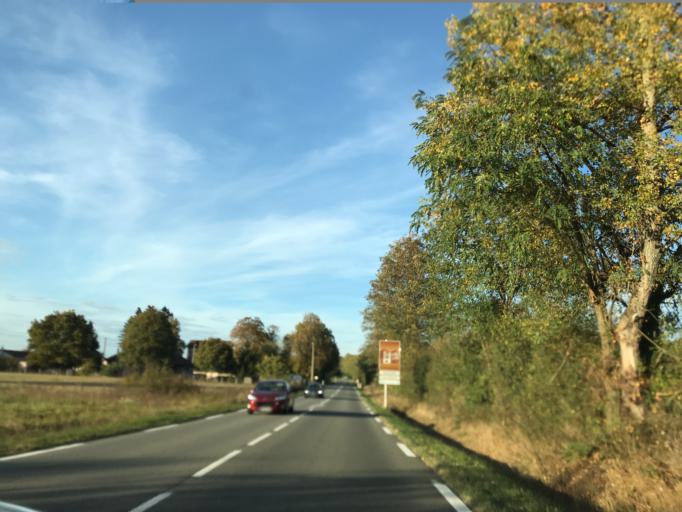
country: FR
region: Auvergne
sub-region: Departement du Puy-de-Dome
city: Puy-Guillaume
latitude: 45.9820
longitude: 3.4843
